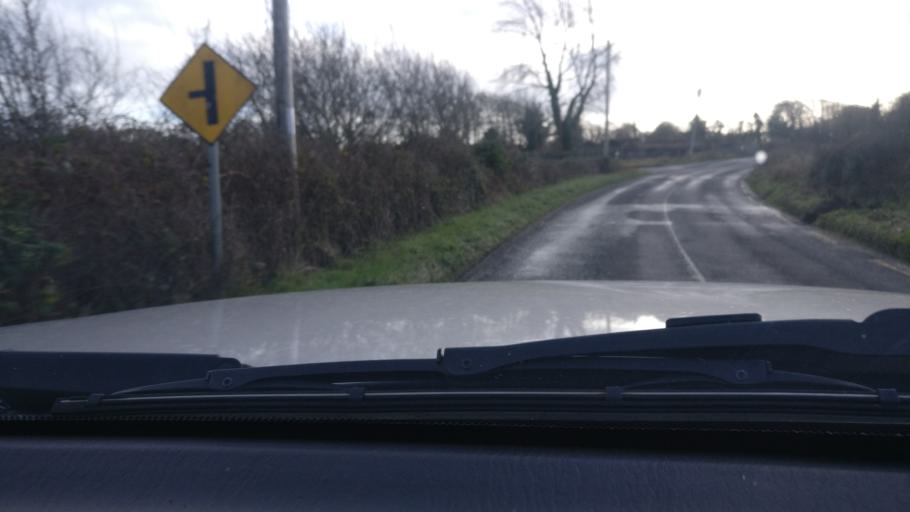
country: IE
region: Connaught
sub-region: County Galway
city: Ballinasloe
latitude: 53.2501
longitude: -8.2636
